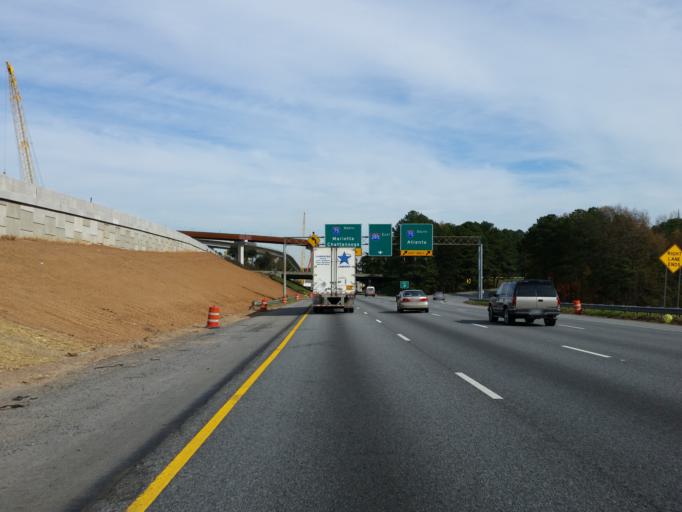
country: US
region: Georgia
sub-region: Cobb County
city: Vinings
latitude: 33.8873
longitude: -84.4650
